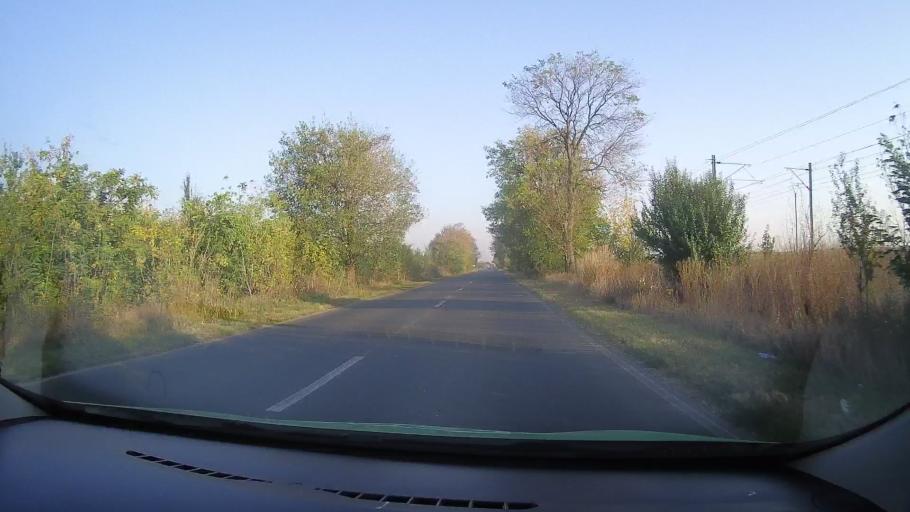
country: RO
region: Arad
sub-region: Comuna Curtici
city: Curtici
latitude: 46.3205
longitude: 21.3067
